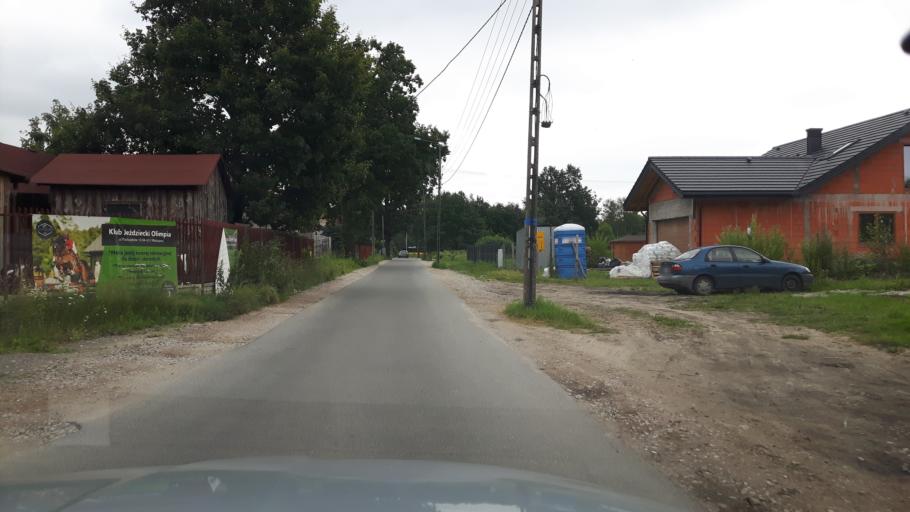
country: PL
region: Masovian Voivodeship
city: Zielonka
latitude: 52.2868
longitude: 21.1706
